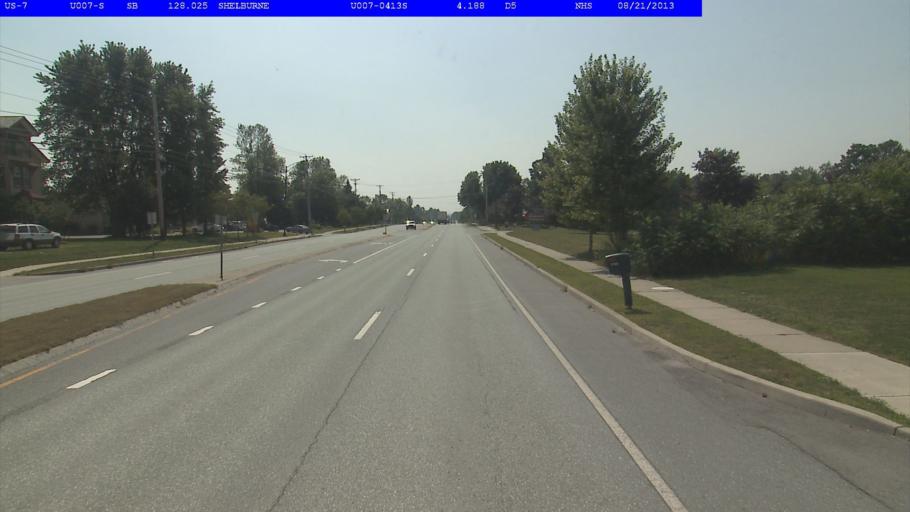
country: US
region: Vermont
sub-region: Chittenden County
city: Burlington
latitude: 44.4021
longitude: -73.2181
